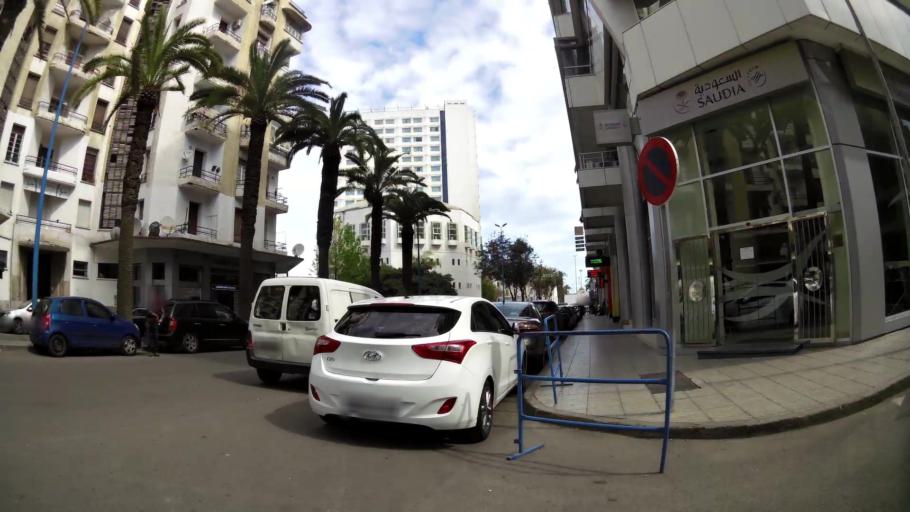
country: MA
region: Grand Casablanca
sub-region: Casablanca
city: Casablanca
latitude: 33.5953
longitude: -7.6100
